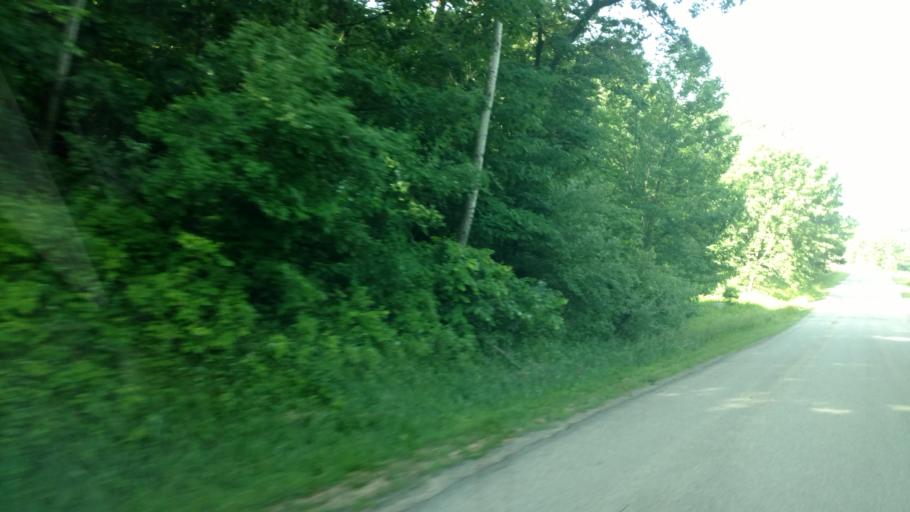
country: US
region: Wisconsin
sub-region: Vernon County
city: Hillsboro
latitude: 43.6011
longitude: -90.2051
